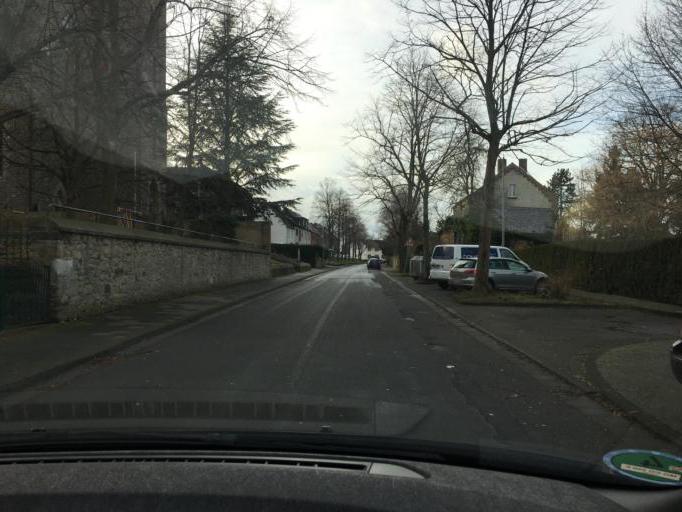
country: DE
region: North Rhine-Westphalia
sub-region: Regierungsbezirk Koln
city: Euskirchen
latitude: 50.6043
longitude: 6.8373
